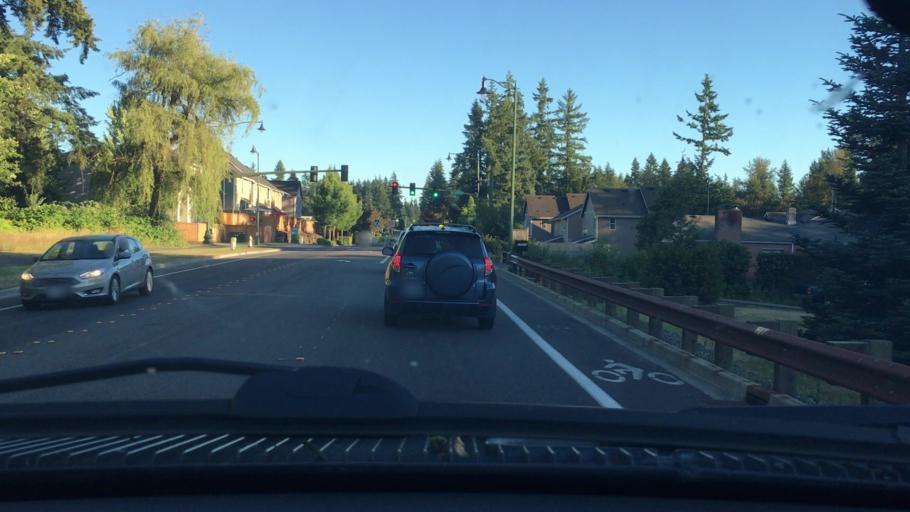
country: US
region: Washington
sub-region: King County
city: Maple Valley
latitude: 47.3876
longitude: -122.0481
